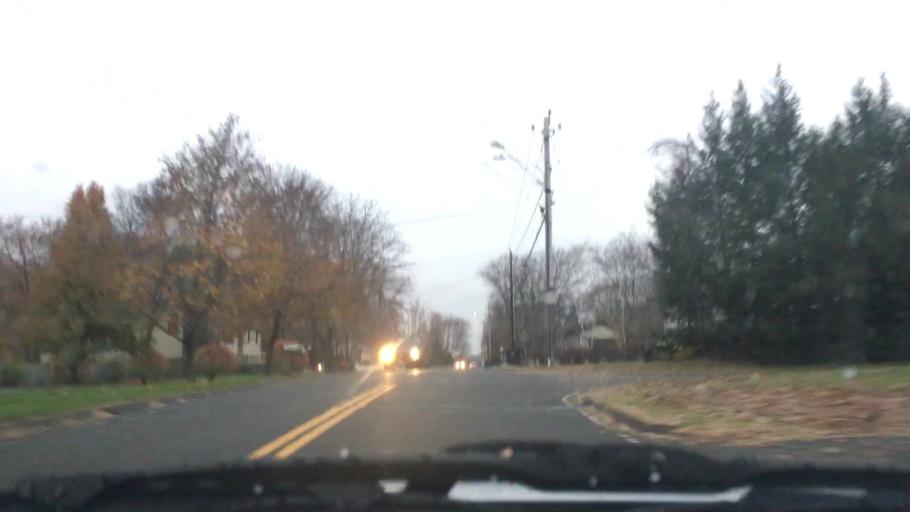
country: US
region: Massachusetts
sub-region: Hampden County
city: Westfield
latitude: 42.1022
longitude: -72.7803
